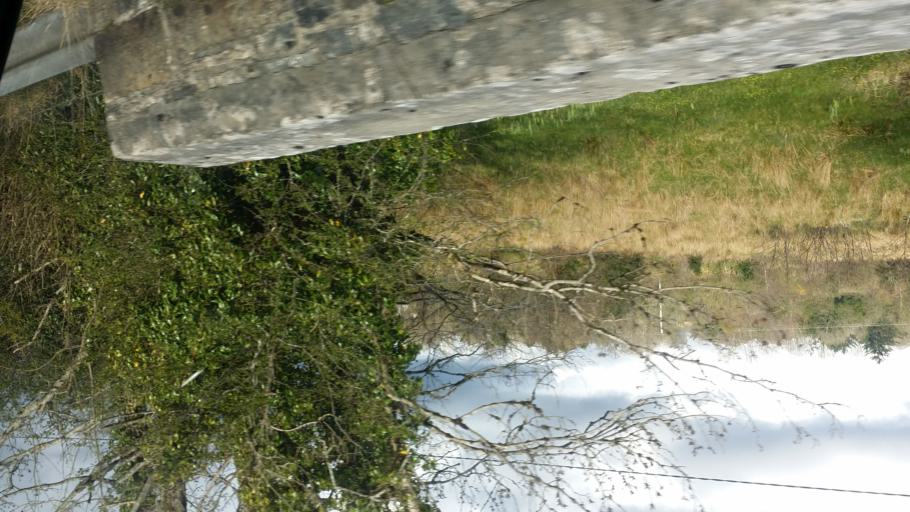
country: IE
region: Connaught
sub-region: County Leitrim
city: Manorhamilton
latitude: 54.3196
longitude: -8.2009
